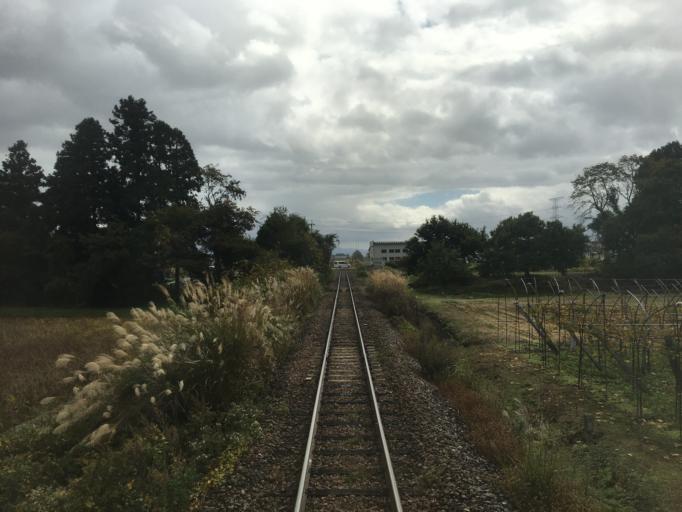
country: JP
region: Yamagata
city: Nagai
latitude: 38.0641
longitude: 140.0366
